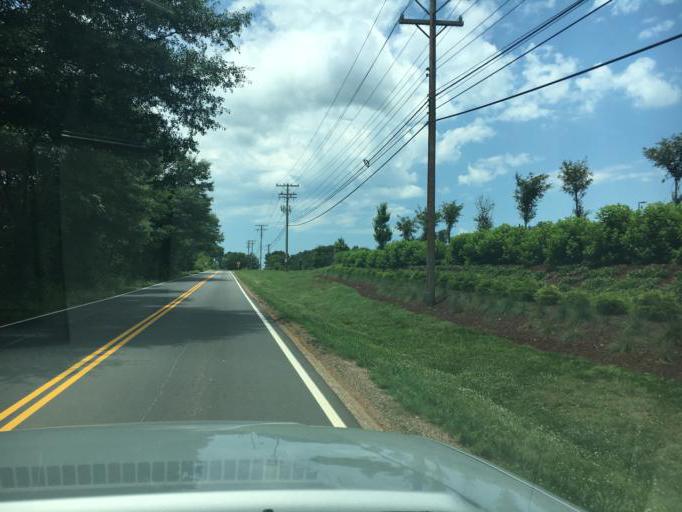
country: US
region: South Carolina
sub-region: Greenville County
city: Five Forks
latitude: 34.8634
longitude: -82.2391
